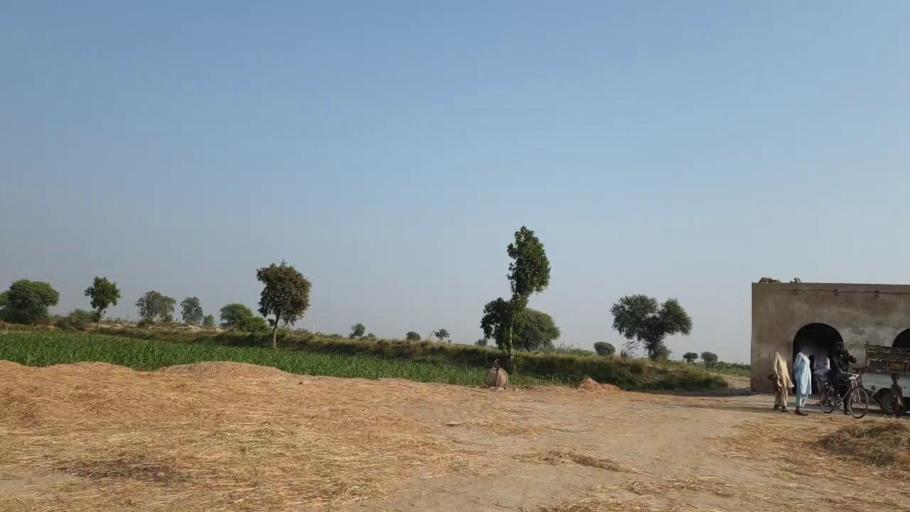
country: PK
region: Sindh
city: Bulri
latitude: 24.9713
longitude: 68.3775
